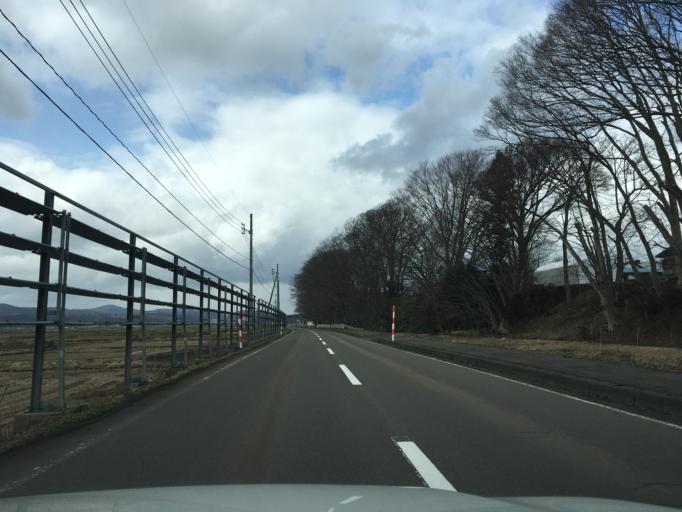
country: JP
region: Akita
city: Takanosu
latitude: 40.1445
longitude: 140.3461
